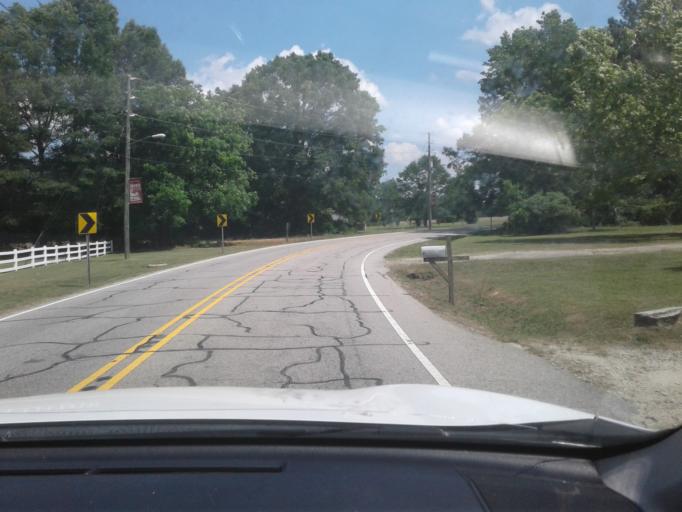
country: US
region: North Carolina
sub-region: Harnett County
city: Erwin
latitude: 35.2156
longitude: -78.6765
